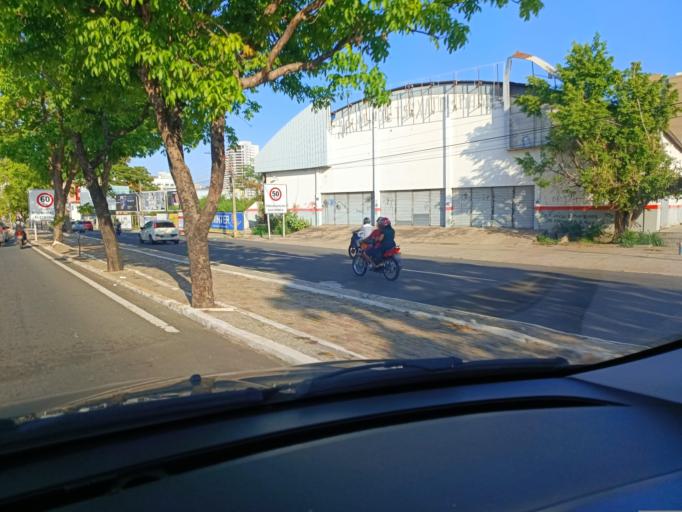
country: BR
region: Piaui
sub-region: Teresina
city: Teresina
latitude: -5.0805
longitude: -42.7826
